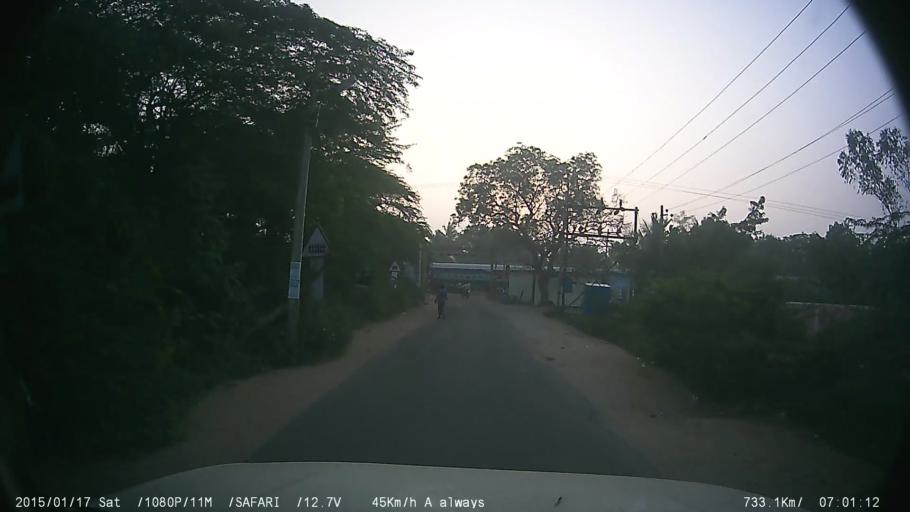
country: IN
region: Tamil Nadu
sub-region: Kancheepuram
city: Singapperumalkovil
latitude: 12.7953
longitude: 80.0179
